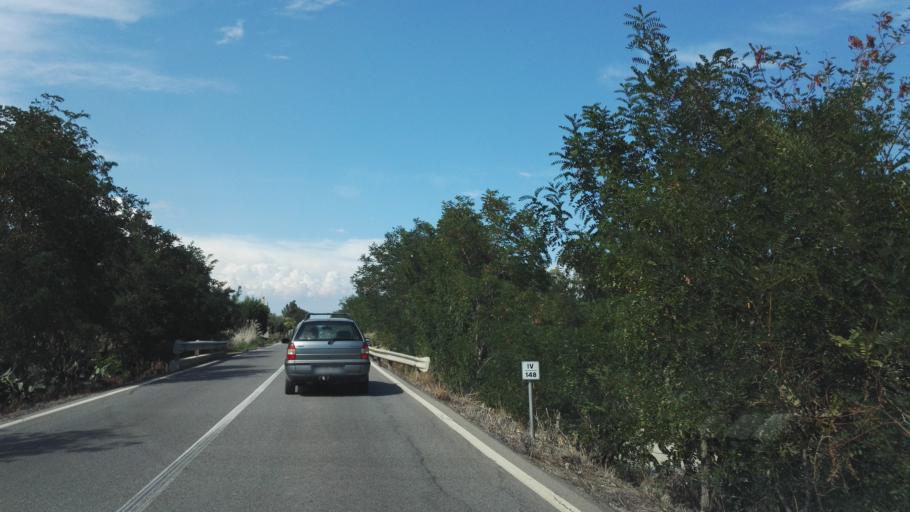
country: IT
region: Calabria
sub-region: Provincia di Catanzaro
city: Santa Caterina dello Ionio Marina
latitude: 38.5515
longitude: 16.5704
